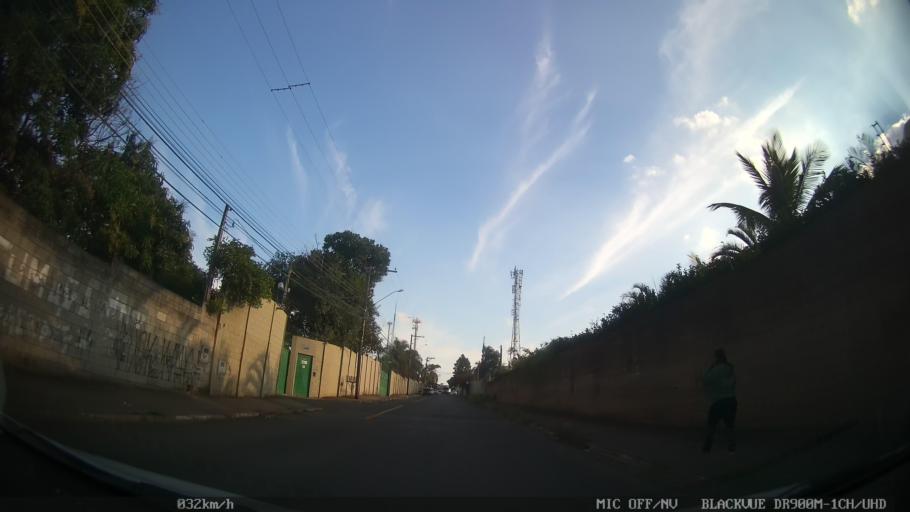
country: BR
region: Sao Paulo
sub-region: Hortolandia
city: Hortolandia
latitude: -22.8629
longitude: -47.1483
